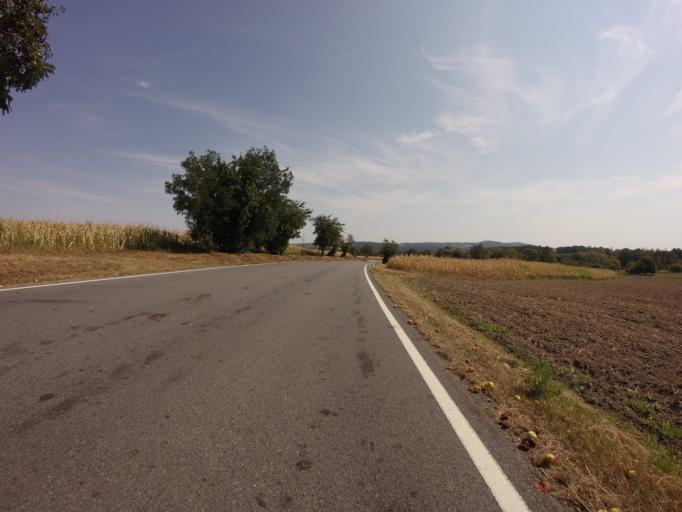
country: CZ
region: Central Bohemia
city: Sedlcany
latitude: 49.6206
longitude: 14.4186
